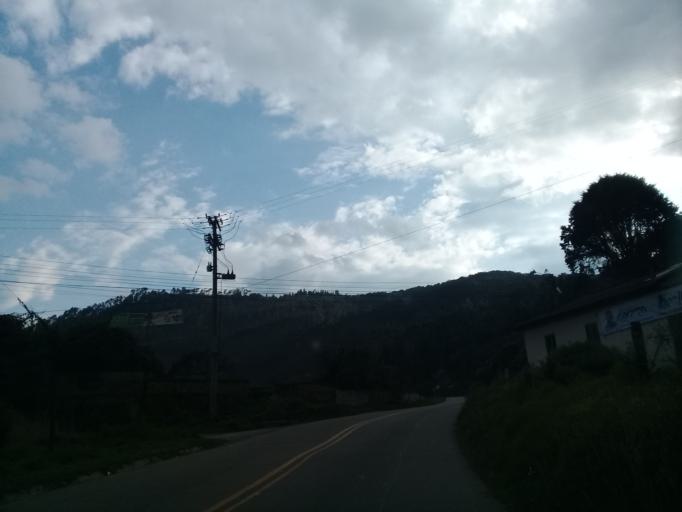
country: CO
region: Cundinamarca
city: Zipaquira
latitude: 5.0264
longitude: -74.0200
